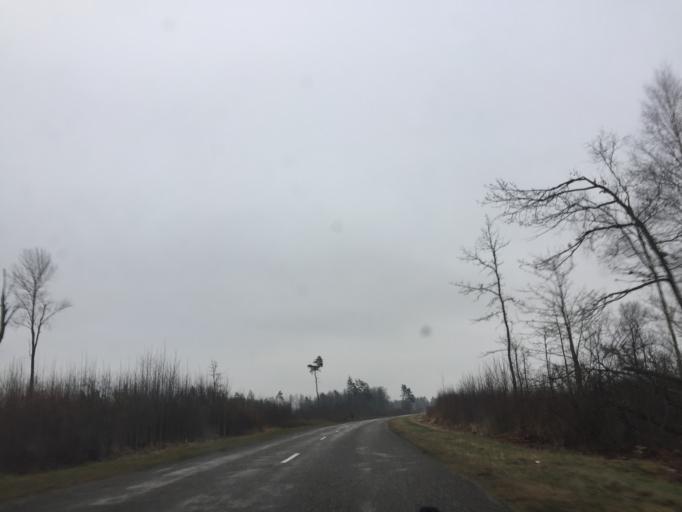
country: LV
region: Limbazu Rajons
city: Limbazi
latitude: 57.5385
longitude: 24.6849
